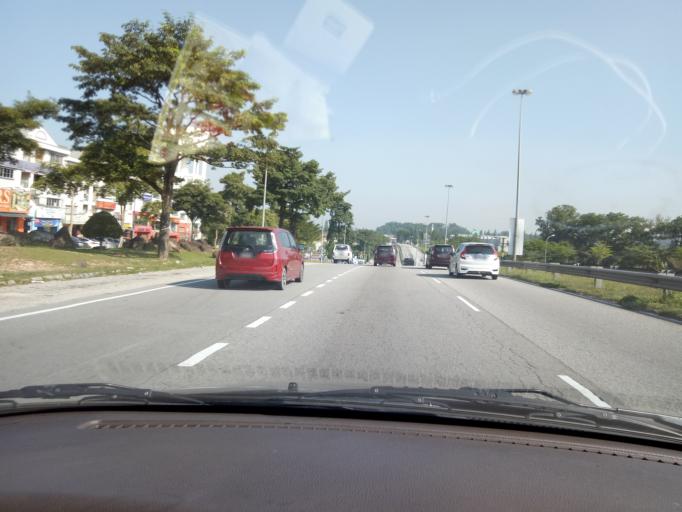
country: MY
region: Selangor
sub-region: Hulu Langat
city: Semenyih
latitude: 2.9936
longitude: 101.8173
